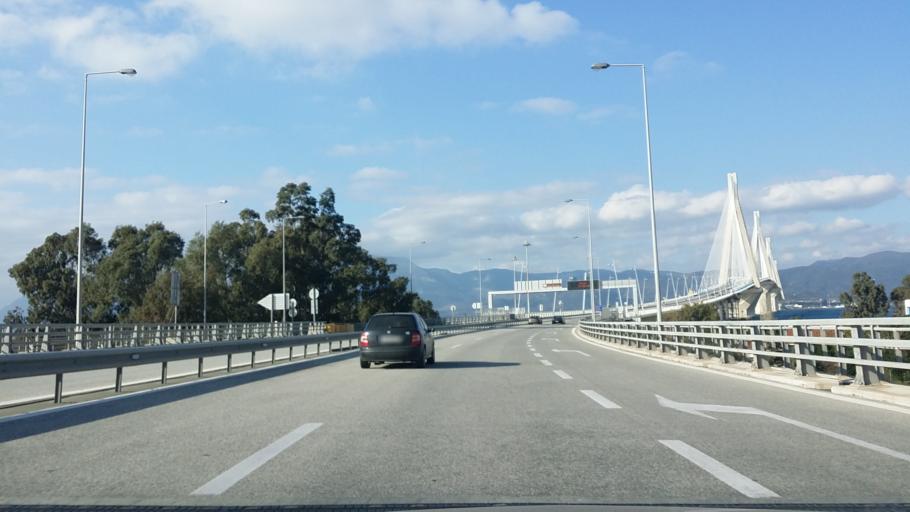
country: GR
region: West Greece
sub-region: Nomos Achaias
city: Rio
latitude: 38.3067
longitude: 21.7815
